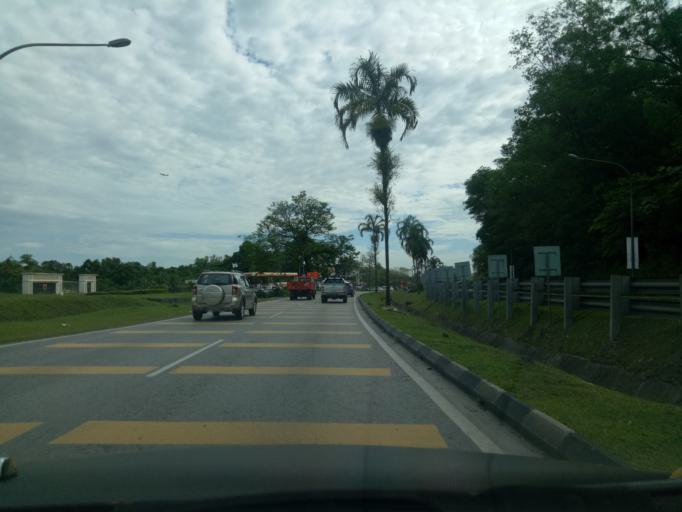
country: MY
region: Sarawak
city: Kuching
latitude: 1.4571
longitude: 110.3250
